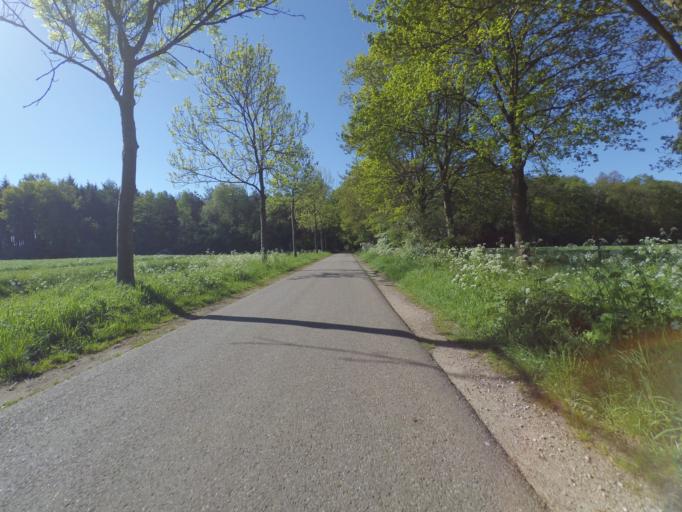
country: NL
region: Gelderland
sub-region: Gemeente Voorst
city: Voorst
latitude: 52.1430
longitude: 6.1278
